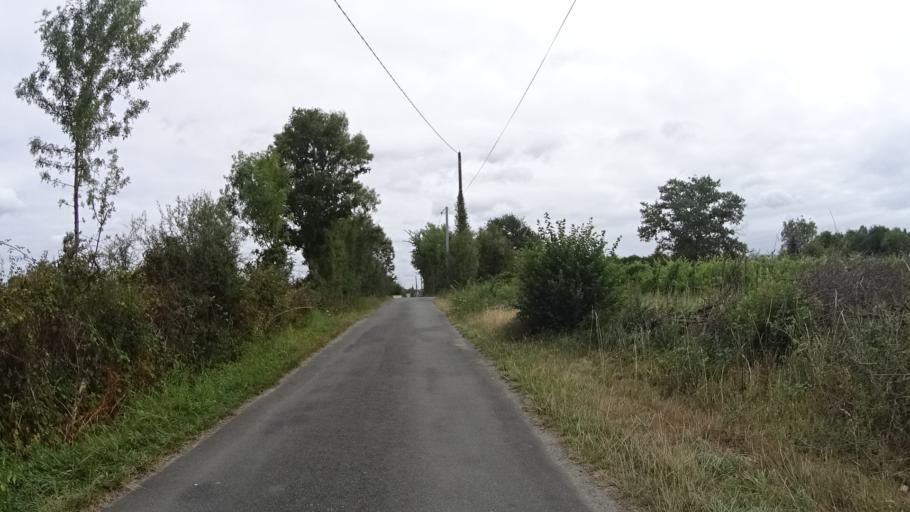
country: FR
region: Pays de la Loire
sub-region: Departement de Maine-et-Loire
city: Savennieres
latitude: 47.3817
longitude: -0.6687
